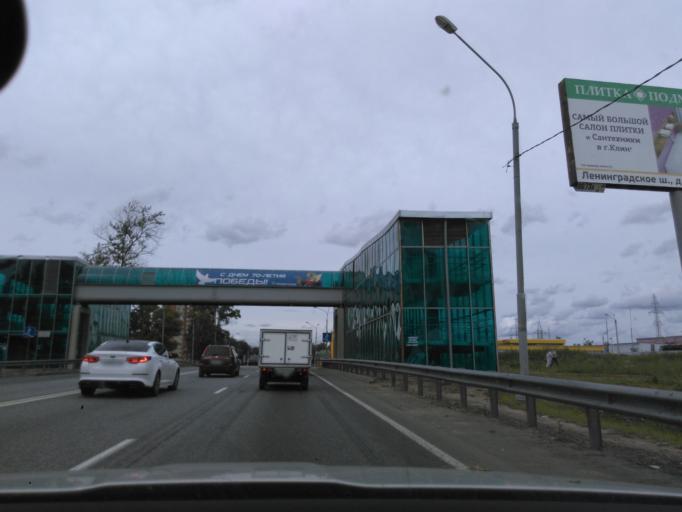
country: RU
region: Moskovskaya
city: Klin
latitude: 56.3204
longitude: 36.7627
